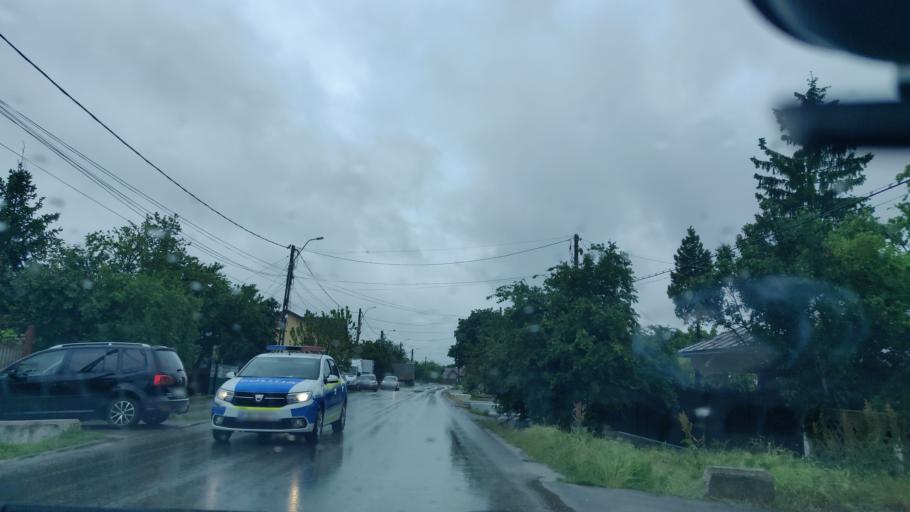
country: RO
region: Giurgiu
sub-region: Comuna Bulbucata
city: Bulbucata
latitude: 44.2788
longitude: 25.8213
